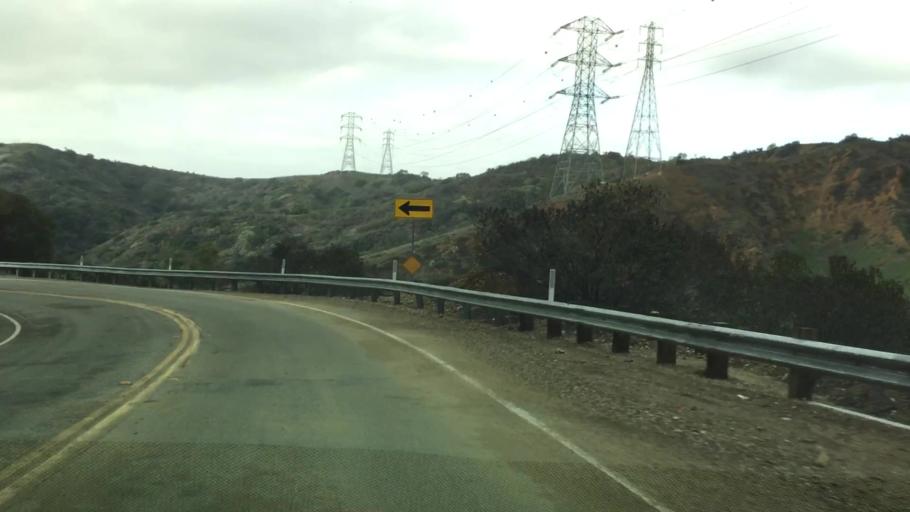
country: US
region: California
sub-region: Los Angeles County
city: Whittier
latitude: 33.9940
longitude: -118.0059
